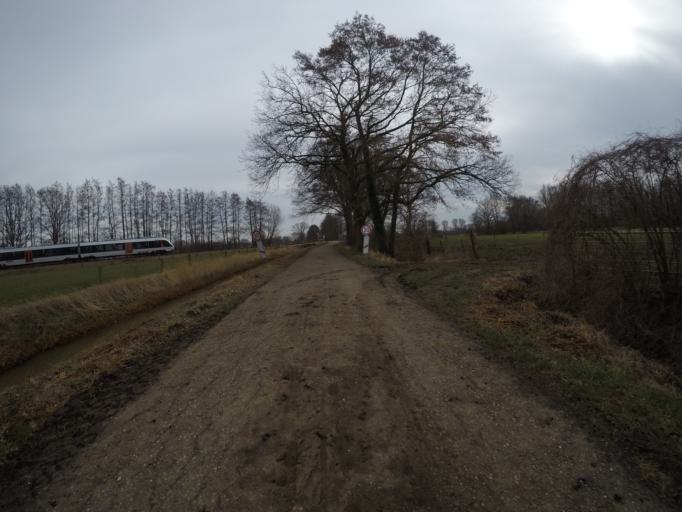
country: DE
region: North Rhine-Westphalia
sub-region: Regierungsbezirk Dusseldorf
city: Hamminkeln
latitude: 51.7512
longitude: 6.6057
